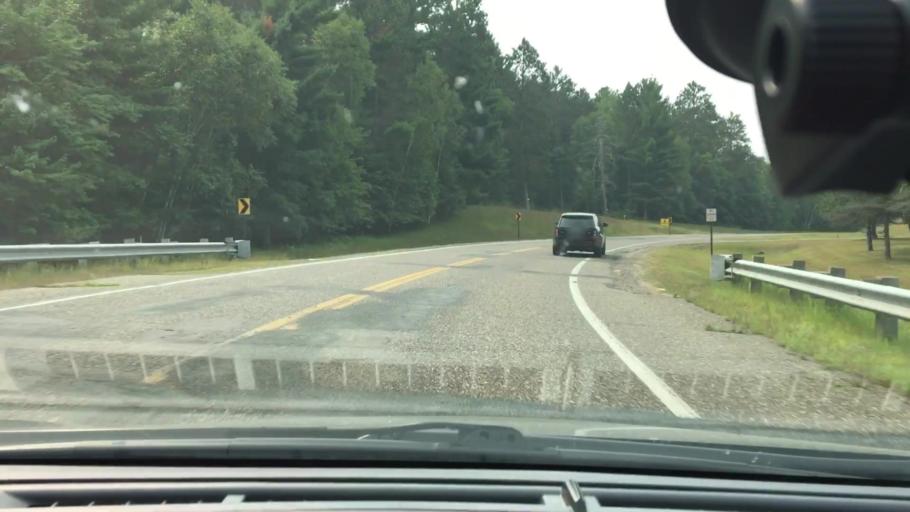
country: US
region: Minnesota
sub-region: Crow Wing County
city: Cross Lake
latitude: 46.6532
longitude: -94.0979
